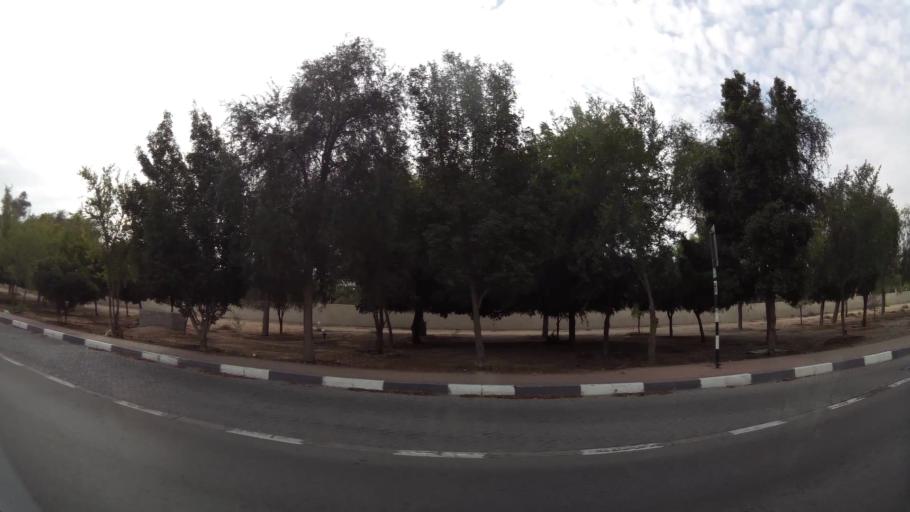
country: AE
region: Abu Dhabi
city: Al Ain
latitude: 24.1767
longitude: 55.6114
